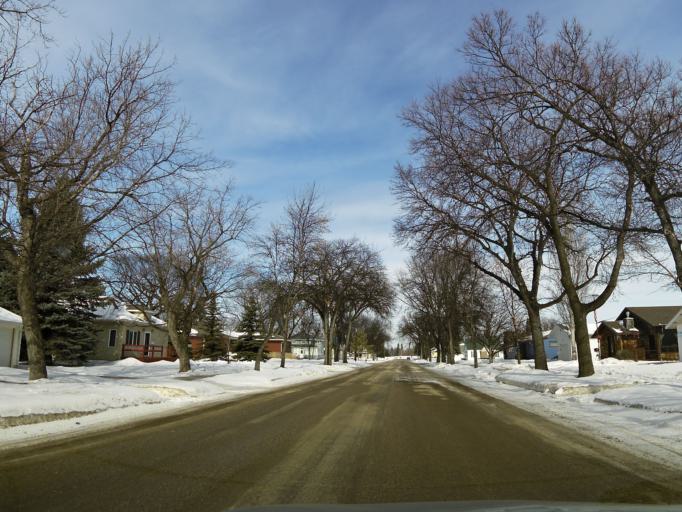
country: US
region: North Dakota
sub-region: Walsh County
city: Grafton
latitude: 48.4166
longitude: -97.4172
